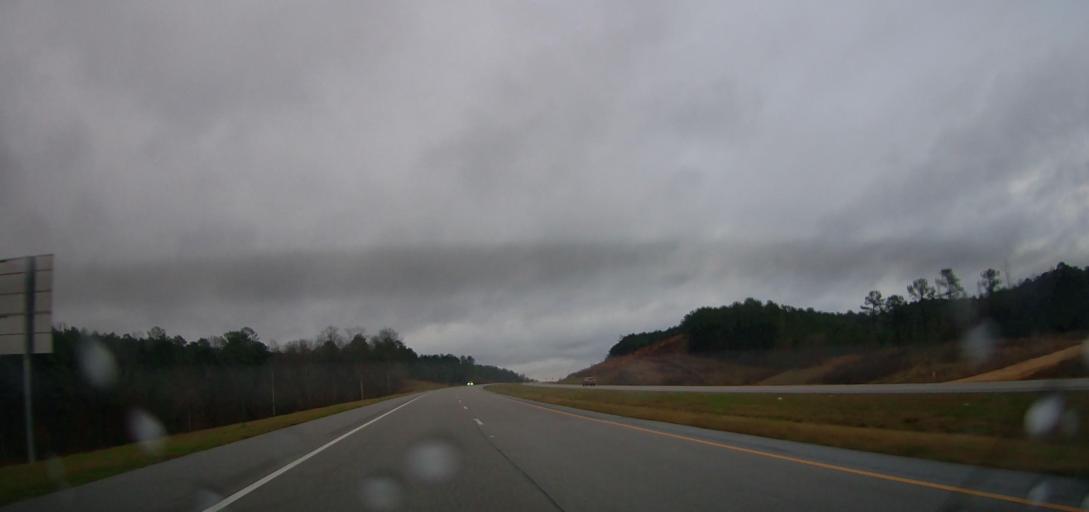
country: US
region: Alabama
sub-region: Bibb County
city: Centreville
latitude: 32.9552
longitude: -87.1185
